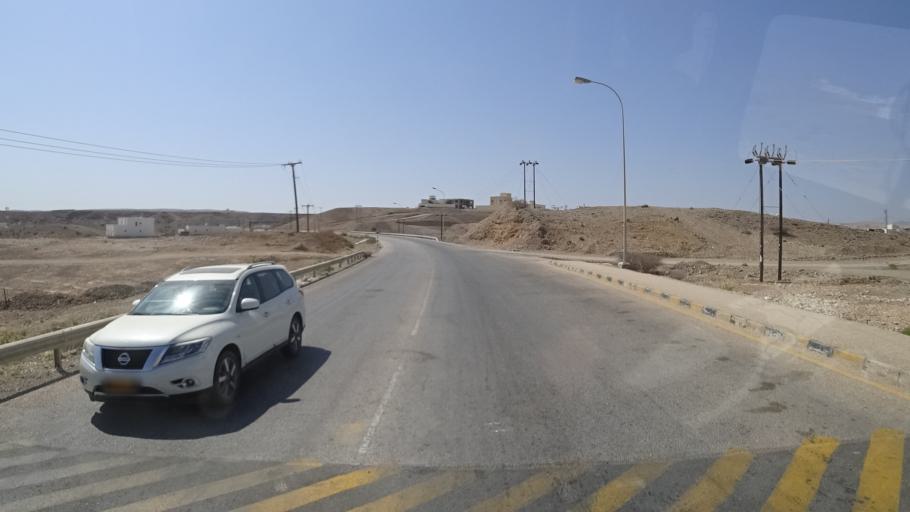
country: OM
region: Ash Sharqiyah
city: Sur
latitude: 22.5450
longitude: 59.5009
